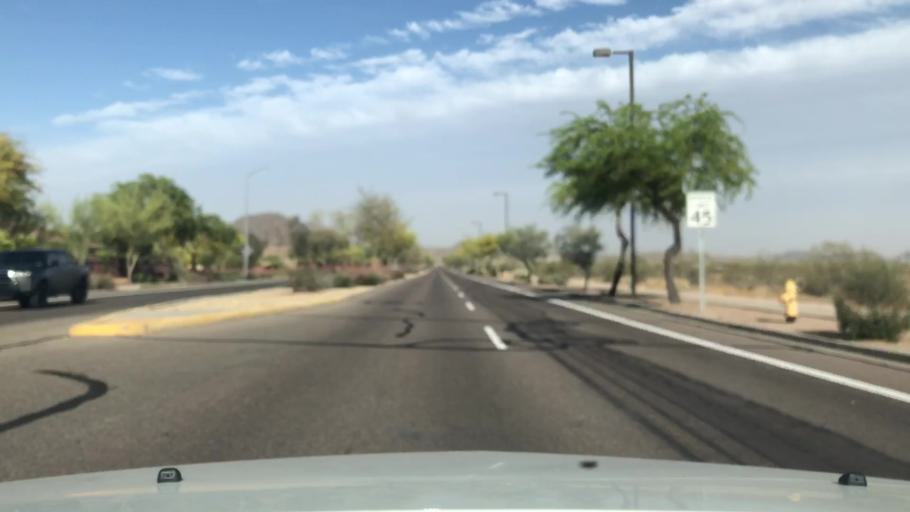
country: US
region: Arizona
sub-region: Maricopa County
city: Anthem
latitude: 33.7257
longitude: -112.1117
